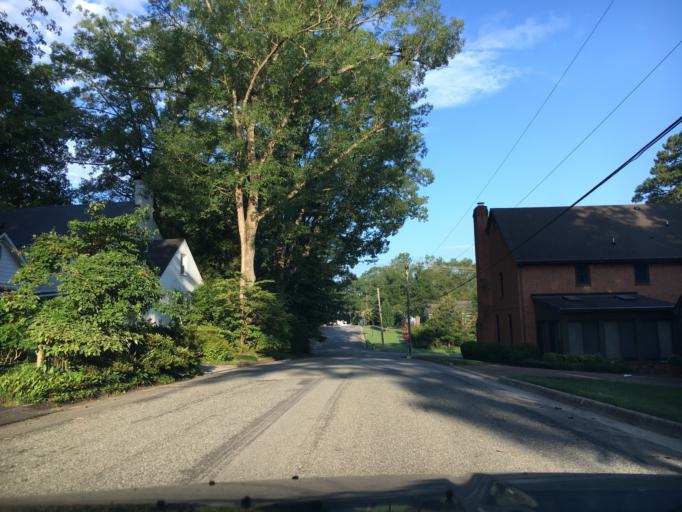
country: US
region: Virginia
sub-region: Halifax County
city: South Boston
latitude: 36.7037
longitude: -78.8918
